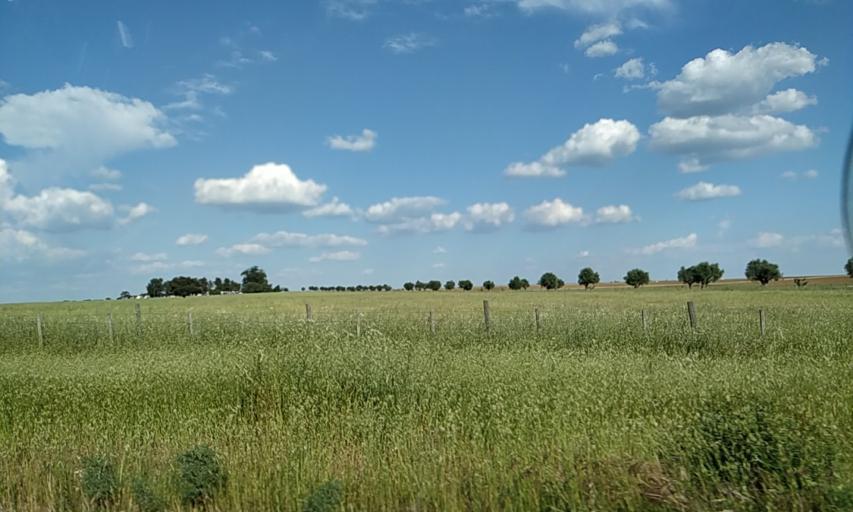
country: PT
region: Evora
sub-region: Estremoz
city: Estremoz
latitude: 38.9832
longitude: -7.4820
